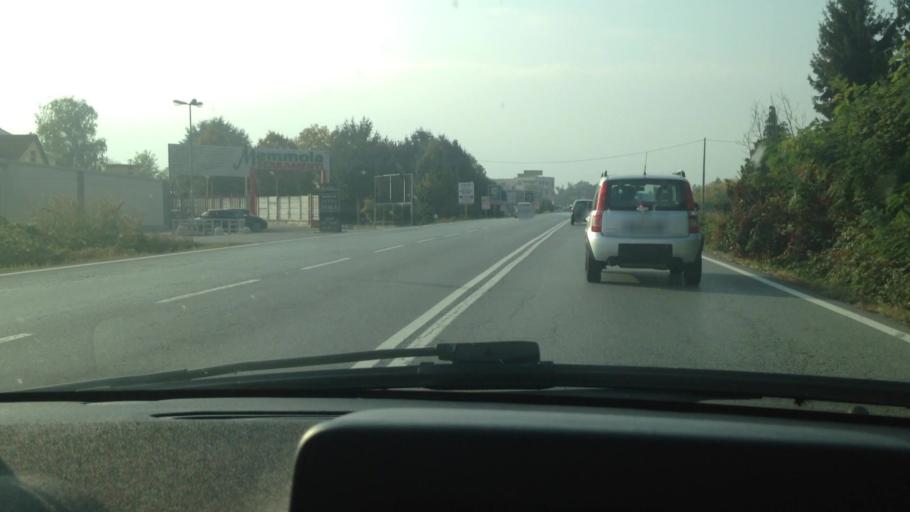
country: IT
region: Piedmont
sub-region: Provincia di Torino
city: Caselle Torinese
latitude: 45.1897
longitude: 7.6367
